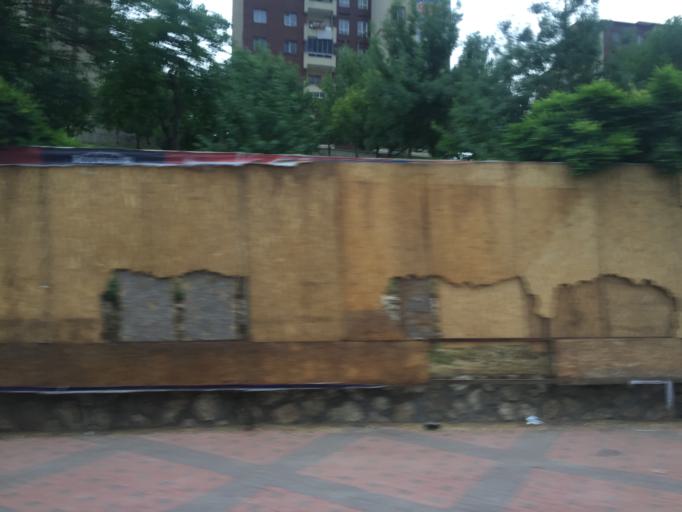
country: TR
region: Gaziantep
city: Gaziantep
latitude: 37.0548
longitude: 37.4166
